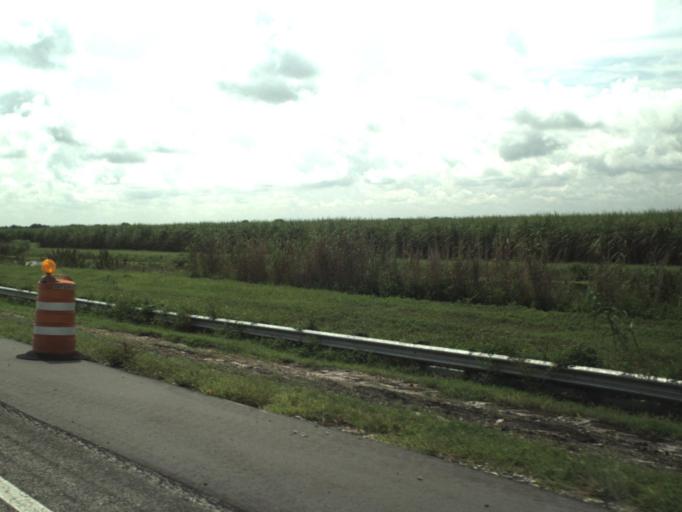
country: US
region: Florida
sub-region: Palm Beach County
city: Belle Glade
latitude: 26.7255
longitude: -80.5119
